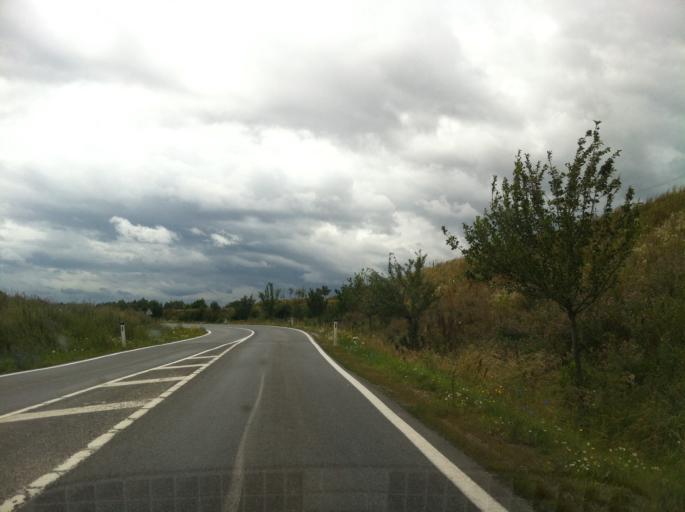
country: AT
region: Lower Austria
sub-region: Politischer Bezirk Tulln
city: Langenrohr
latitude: 48.2943
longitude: 16.0107
